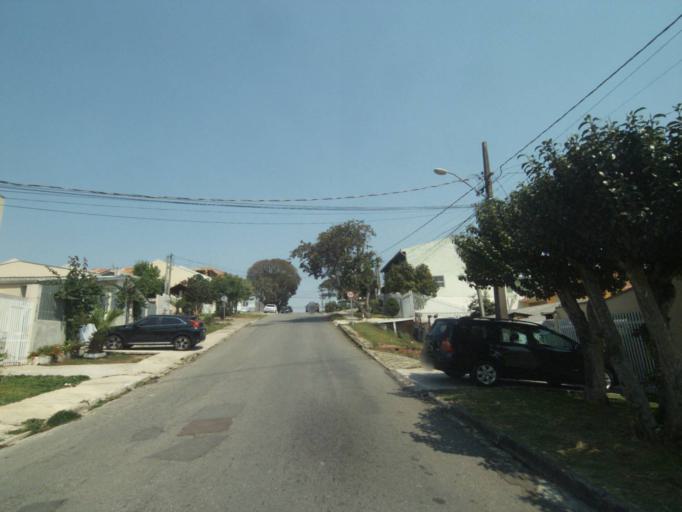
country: BR
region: Parana
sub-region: Sao Jose Dos Pinhais
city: Sao Jose dos Pinhais
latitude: -25.5093
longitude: -49.2662
